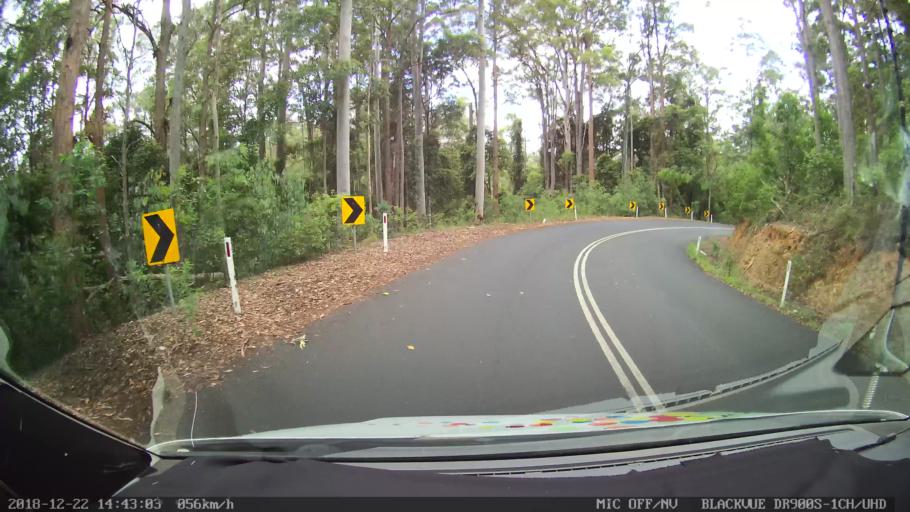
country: AU
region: New South Wales
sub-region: Bellingen
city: Dorrigo
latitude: -30.1640
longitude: 152.5856
